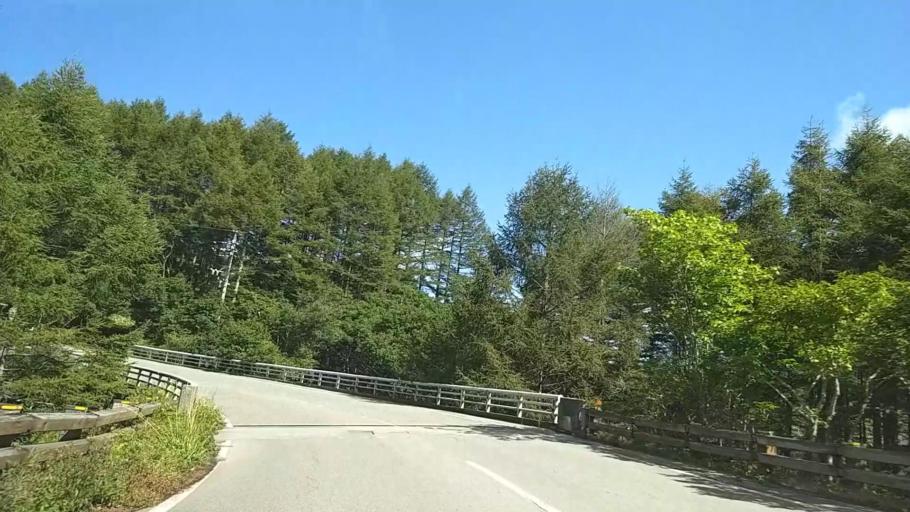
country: JP
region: Nagano
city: Suwa
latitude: 36.1115
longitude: 138.1706
